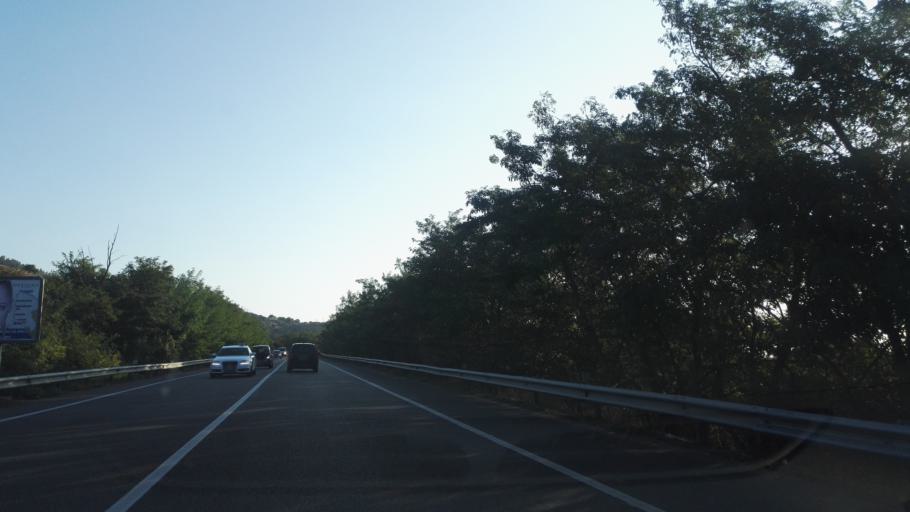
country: IT
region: Calabria
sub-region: Provincia di Catanzaro
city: Montepaone Lido
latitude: 38.7351
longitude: 16.5438
